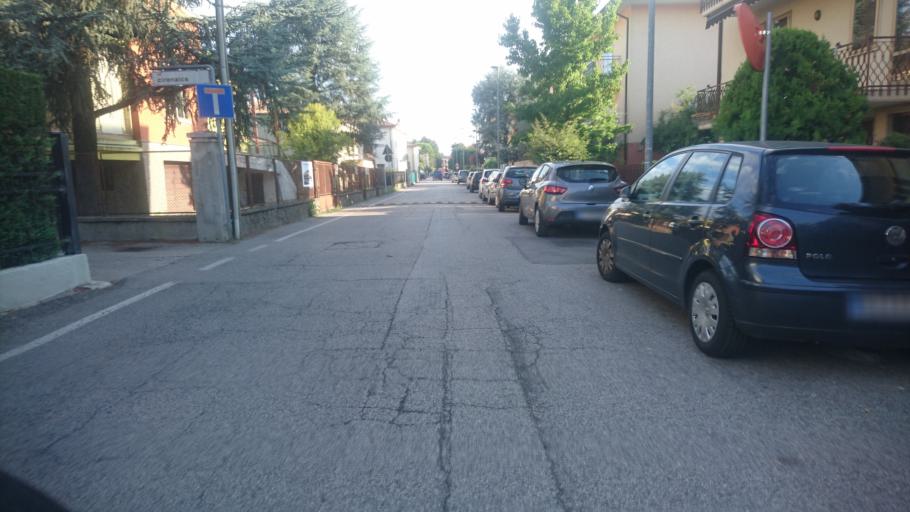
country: IT
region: Veneto
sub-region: Provincia di Padova
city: Mandriola-Sant'Agostino
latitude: 45.3975
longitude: 11.8561
